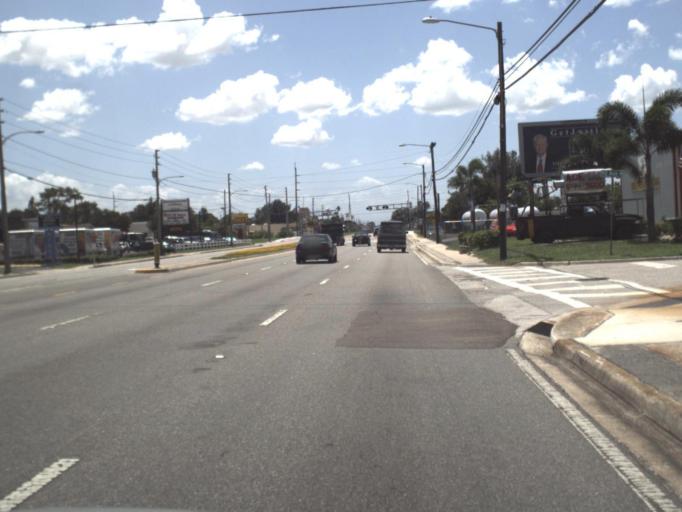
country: US
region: Florida
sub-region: Pinellas County
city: Pinellas Park
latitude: 27.8555
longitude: -82.7289
